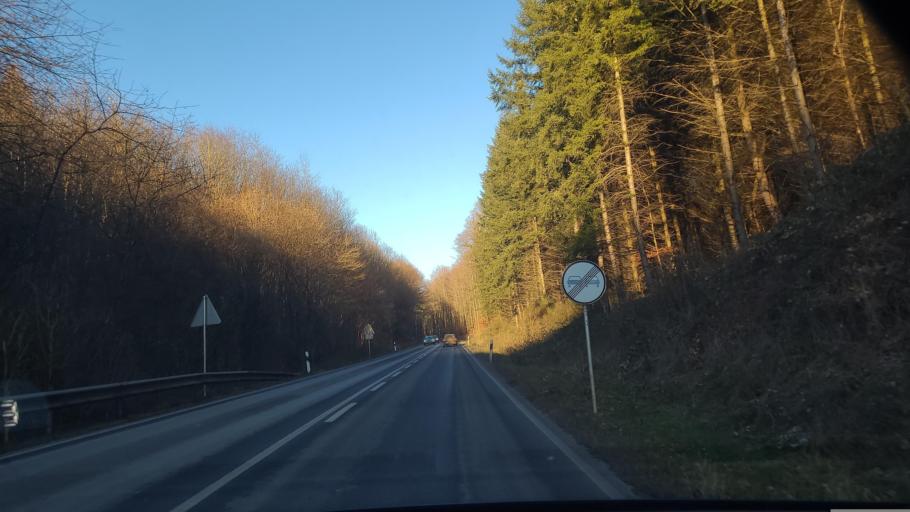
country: LU
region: Luxembourg
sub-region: Canton de Luxembourg
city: Strassen
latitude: 49.6350
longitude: 6.0837
